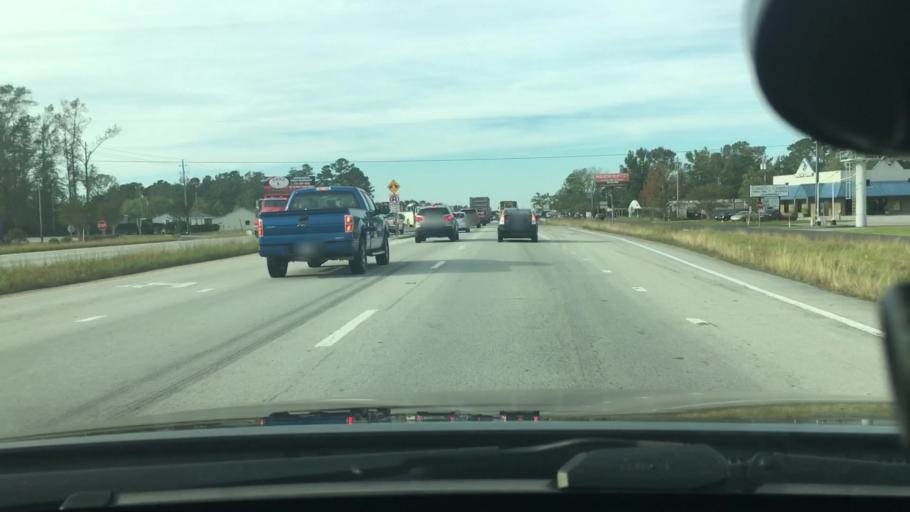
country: US
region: North Carolina
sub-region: Craven County
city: James City
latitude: 35.0643
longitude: -77.0220
